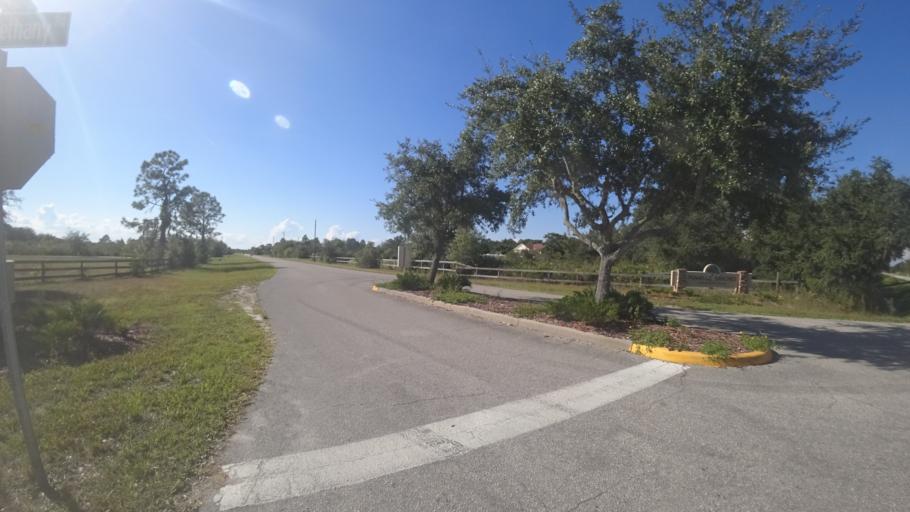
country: US
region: Florida
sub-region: Sarasota County
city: The Meadows
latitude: 27.4159
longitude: -82.2710
